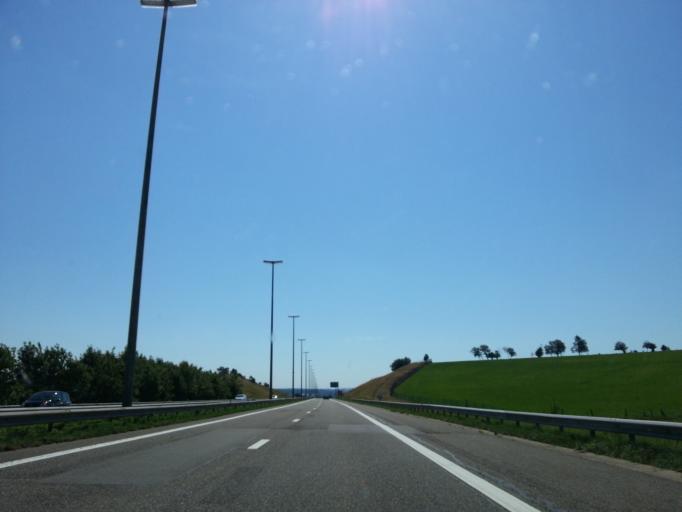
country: BE
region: Wallonia
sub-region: Province de Liege
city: Saint-Vith
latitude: 50.2951
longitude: 6.0860
